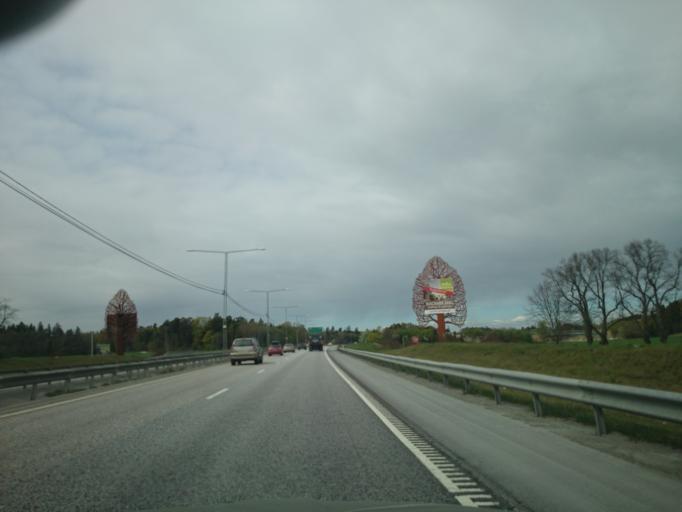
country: SE
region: Stockholm
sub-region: Upplands Vasby Kommun
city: Upplands Vaesby
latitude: 59.5339
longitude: 17.9161
